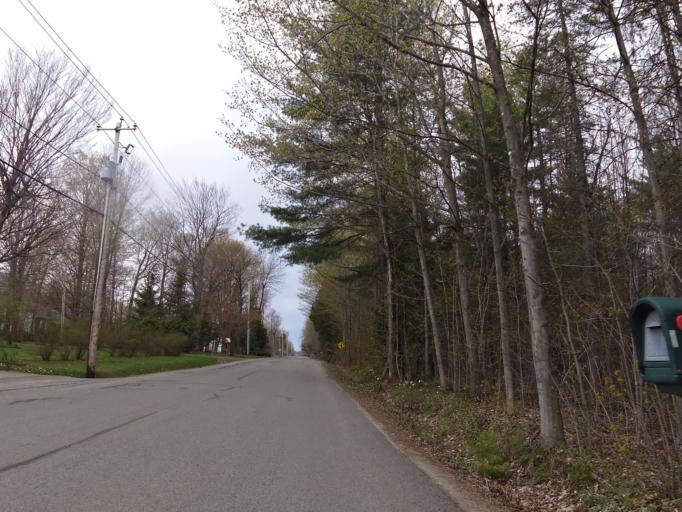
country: CA
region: Ontario
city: Hawkesbury
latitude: 45.6241
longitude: -74.5712
